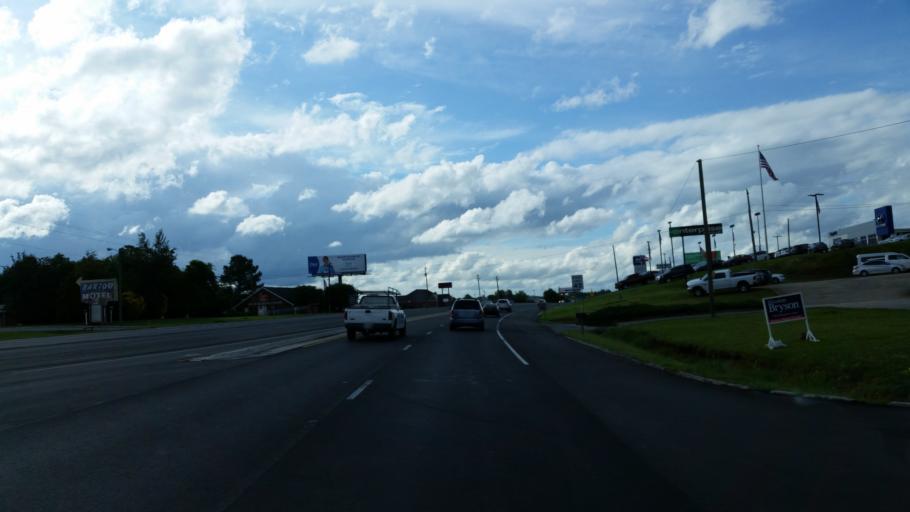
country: US
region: Georgia
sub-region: Bartow County
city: Cartersville
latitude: 34.1899
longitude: -84.7881
